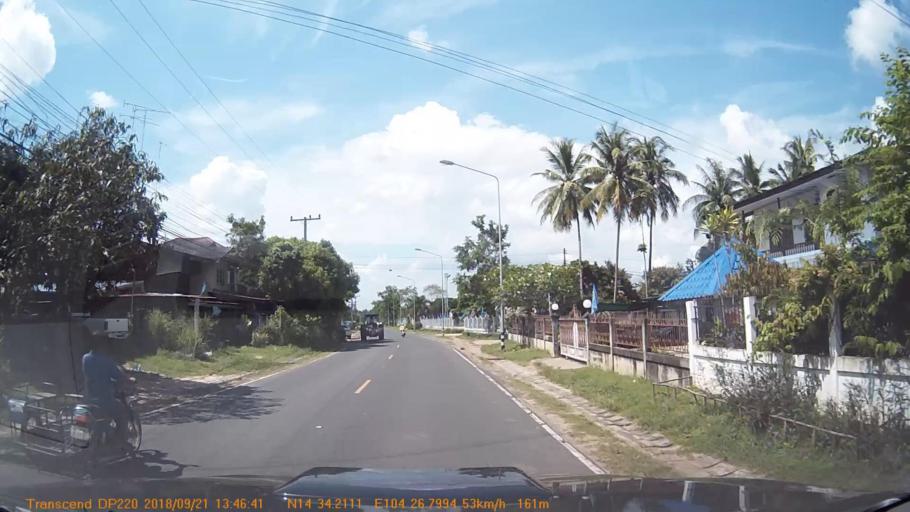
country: TH
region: Sisaket
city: Khun Han
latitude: 14.5706
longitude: 104.4466
